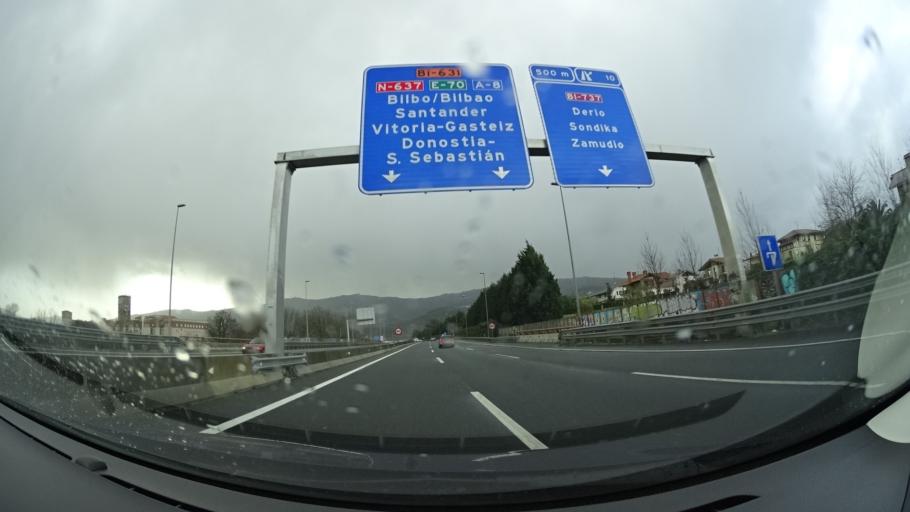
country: ES
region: Basque Country
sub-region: Bizkaia
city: Derio
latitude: 43.2958
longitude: -2.8819
